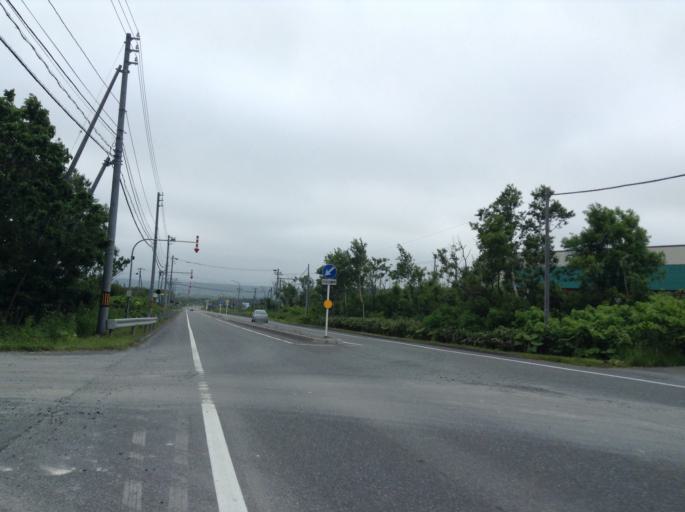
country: JP
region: Hokkaido
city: Wakkanai
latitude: 45.3727
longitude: 141.7187
